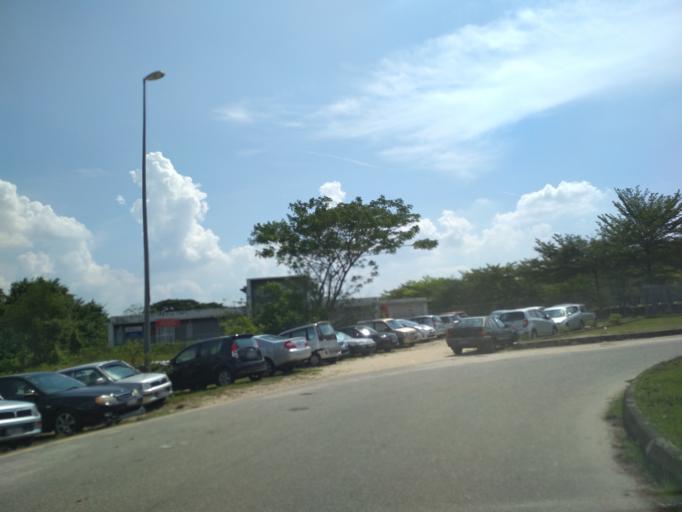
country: MY
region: Perak
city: Kampar
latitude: 4.3368
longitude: 101.1455
